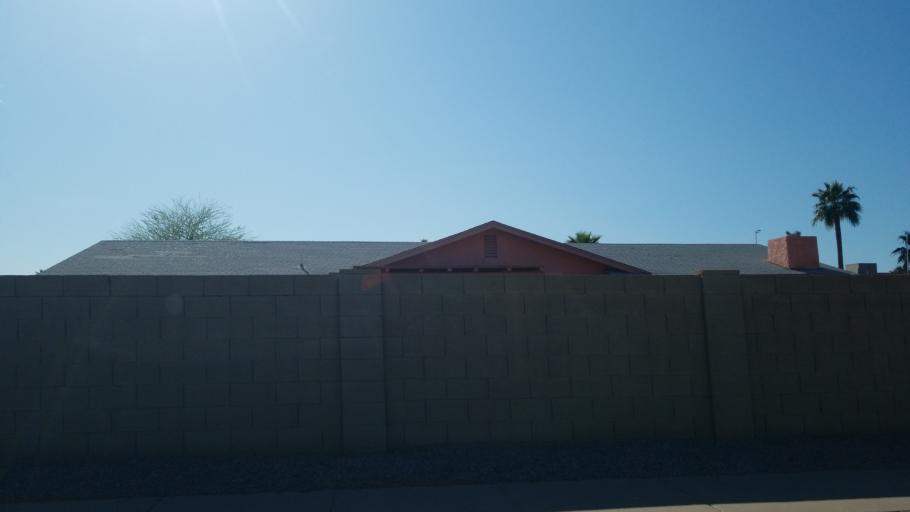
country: US
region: Arizona
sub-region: Maricopa County
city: Glendale
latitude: 33.5640
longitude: -112.1777
